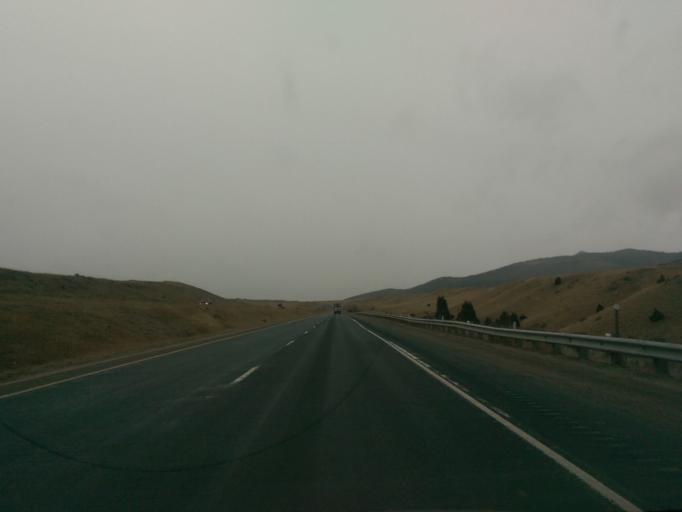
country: US
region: Montana
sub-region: Jefferson County
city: Whitehall
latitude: 45.8980
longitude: -111.8280
